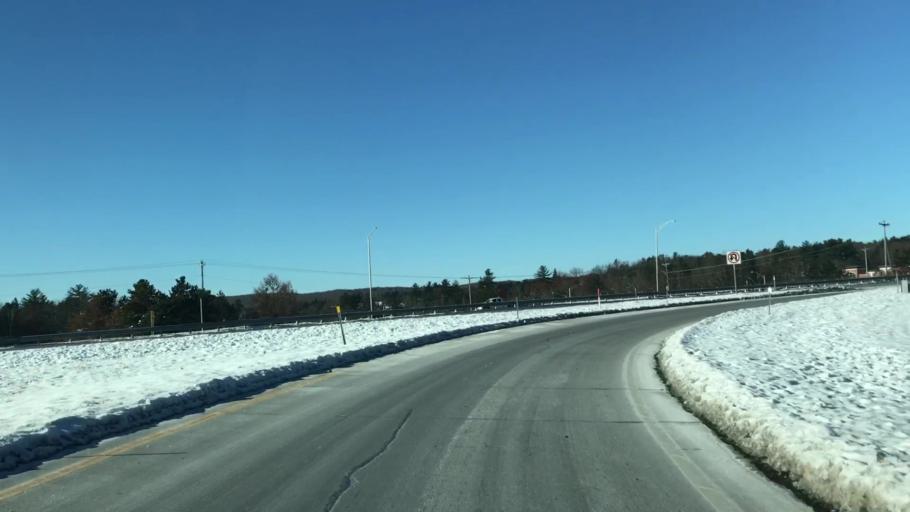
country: US
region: New Hampshire
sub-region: Merrimack County
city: South Hooksett
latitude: 43.0436
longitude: -71.4632
